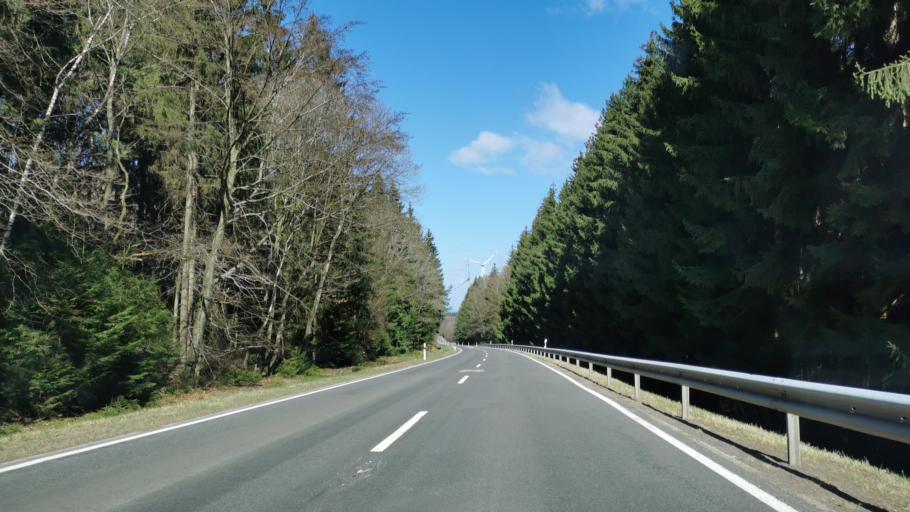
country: DE
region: Rheinland-Pfalz
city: Horath
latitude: 49.8334
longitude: 6.9871
